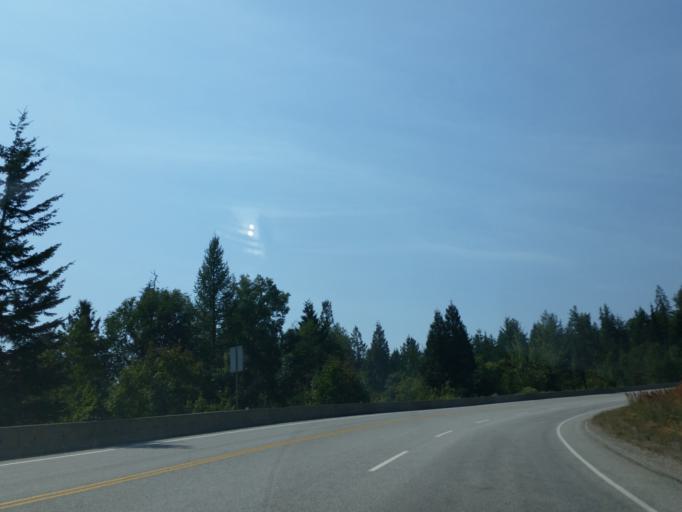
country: CA
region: British Columbia
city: Castlegar
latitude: 49.2907
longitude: -117.6569
